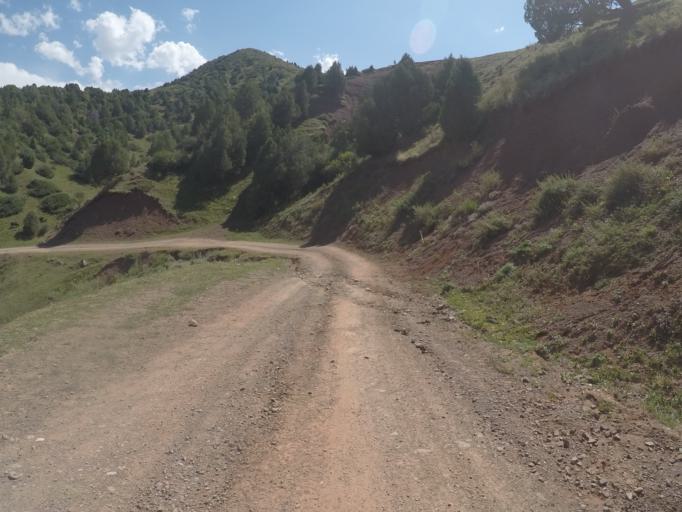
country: KG
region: Chuy
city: Bishkek
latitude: 42.6470
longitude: 74.5657
